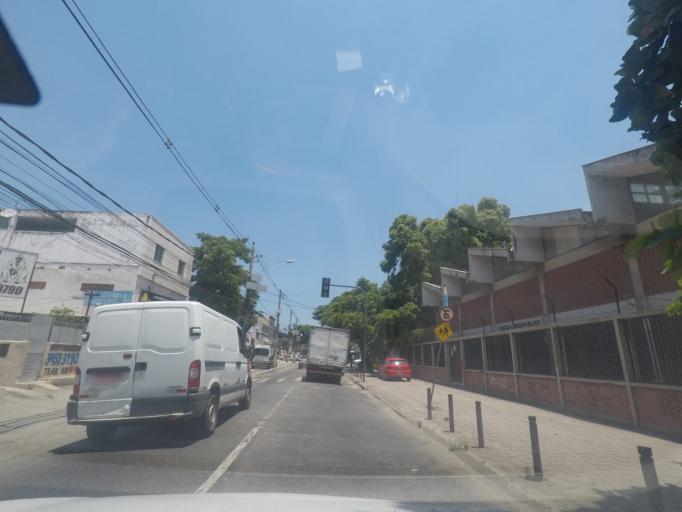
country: BR
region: Rio de Janeiro
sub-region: Duque De Caxias
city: Duque de Caxias
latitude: -22.8177
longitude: -43.3036
